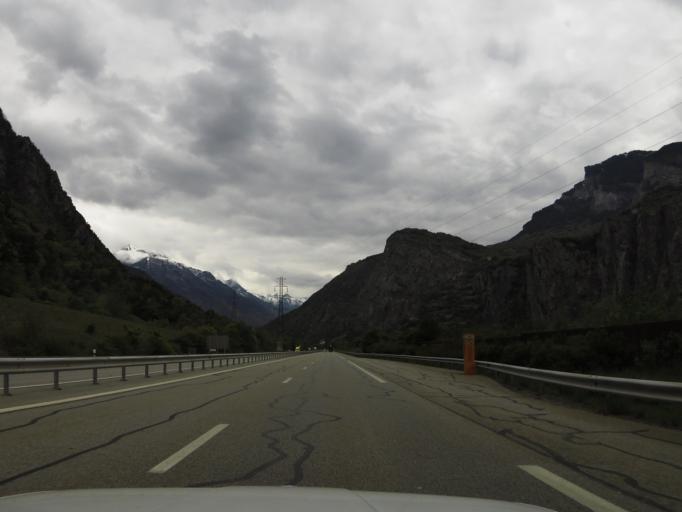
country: FR
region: Rhone-Alpes
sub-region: Departement de la Savoie
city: Saint-Jean-de-Maurienne
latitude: 45.3063
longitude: 6.3444
